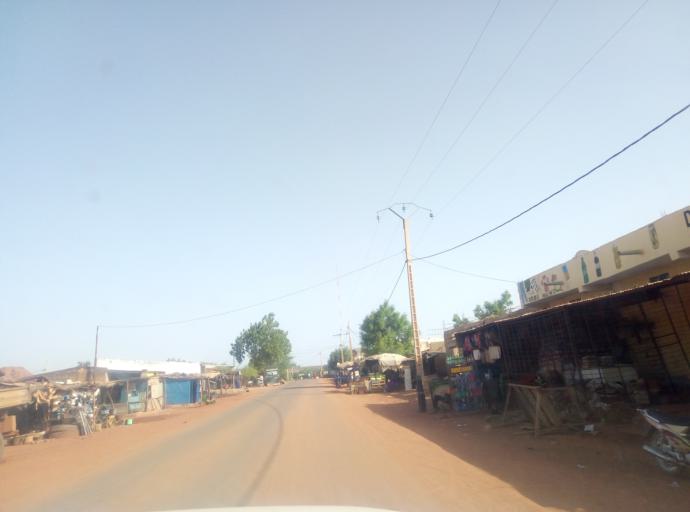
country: ML
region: Bamako
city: Bamako
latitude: 12.6142
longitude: -7.7772
